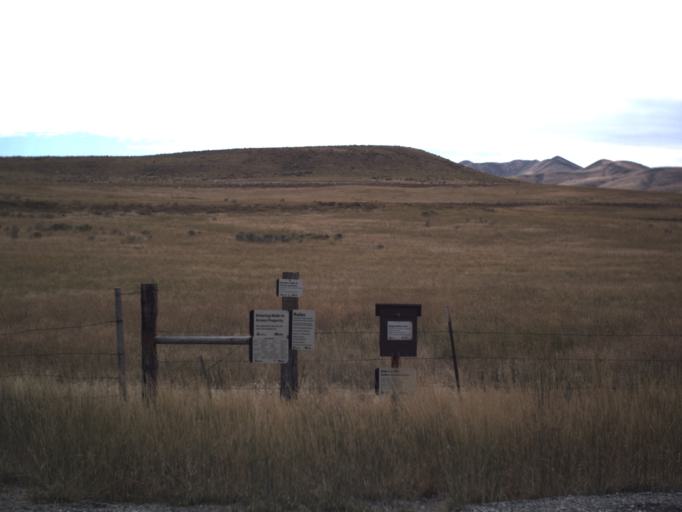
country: US
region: Utah
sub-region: Box Elder County
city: Garland
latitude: 41.8840
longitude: -112.4905
